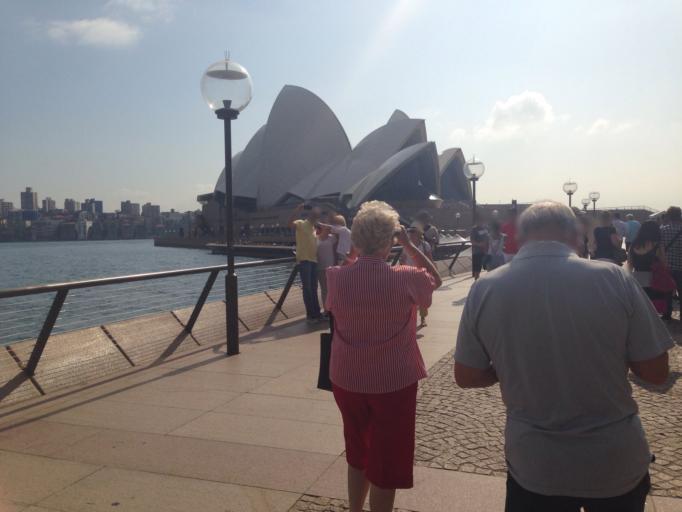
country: AU
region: New South Wales
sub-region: North Sydney
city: Kirribilli
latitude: -33.8587
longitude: 151.2133
